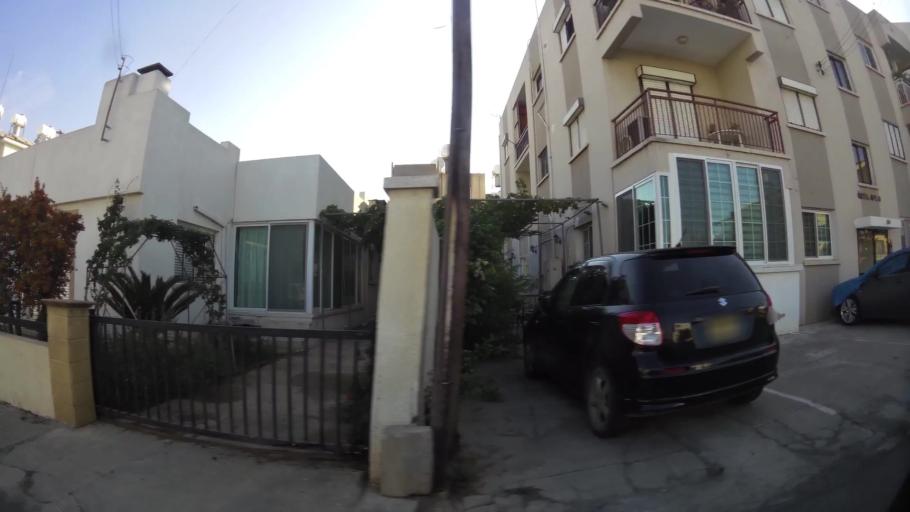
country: CY
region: Lefkosia
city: Nicosia
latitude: 35.2031
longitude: 33.3498
